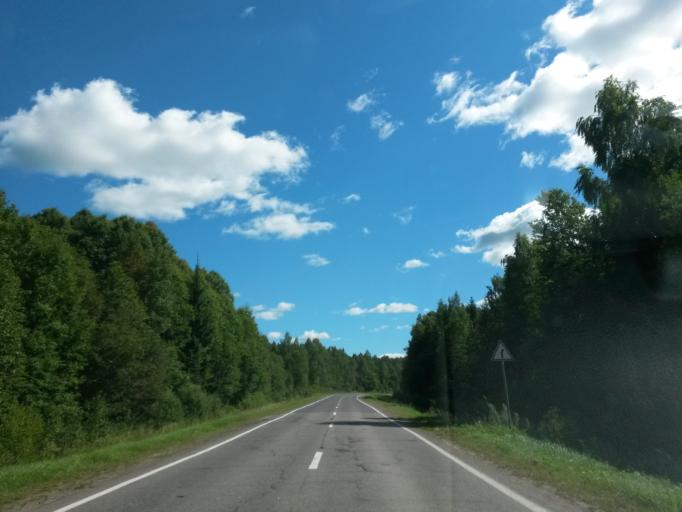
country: RU
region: Jaroslavl
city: Konstantinovskiy
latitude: 57.8584
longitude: 39.6163
